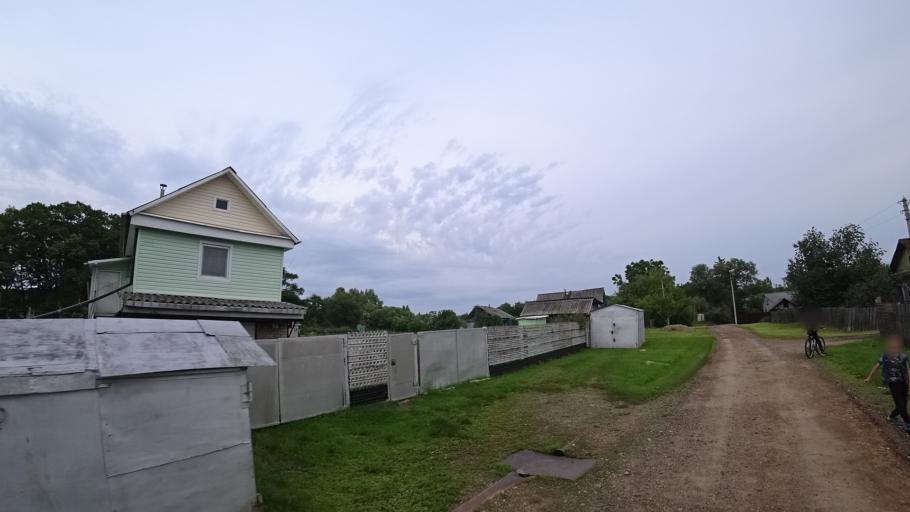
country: RU
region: Primorskiy
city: Novosysoyevka
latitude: 44.2239
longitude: 133.3541
